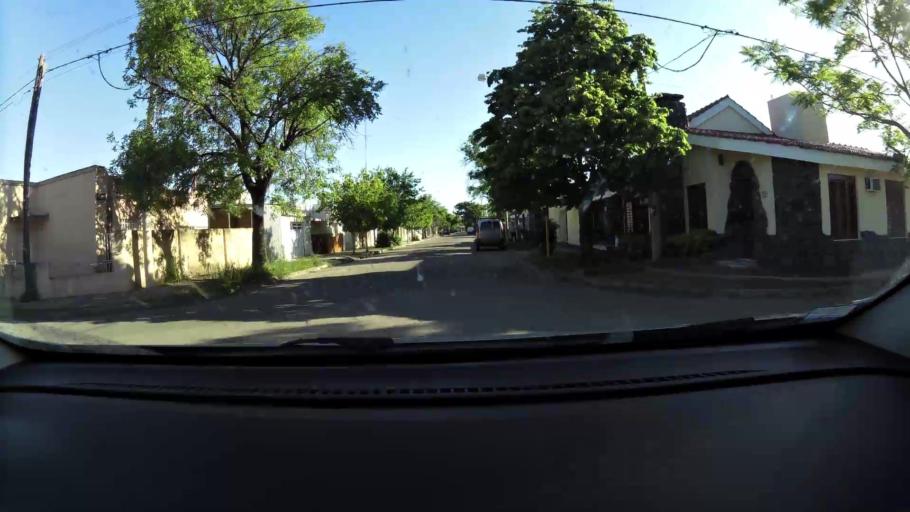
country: AR
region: Cordoba
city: San Francisco
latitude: -31.4382
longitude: -62.0914
